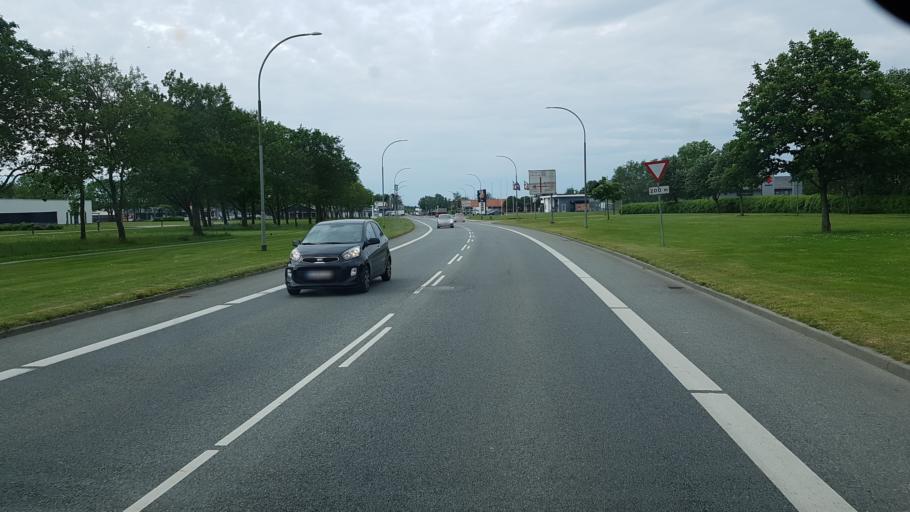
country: DK
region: South Denmark
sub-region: Varde Kommune
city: Varde
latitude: 55.6280
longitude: 8.4628
